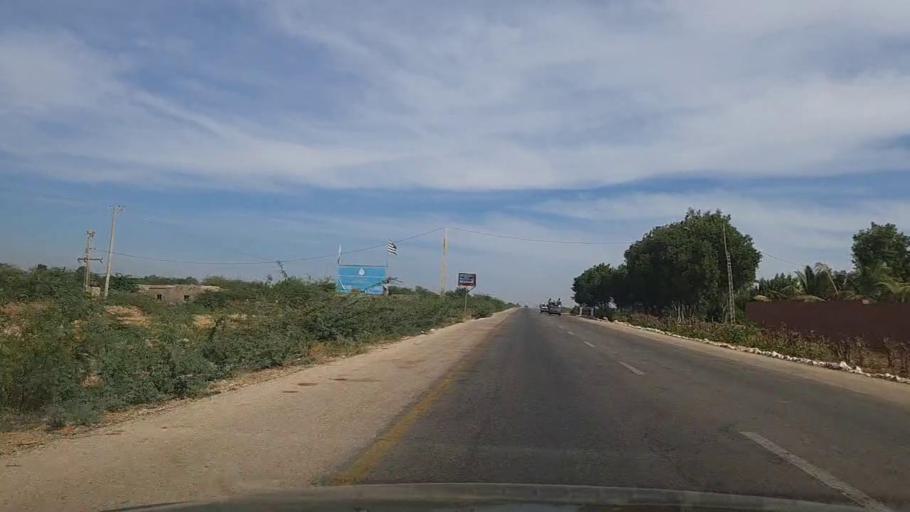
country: PK
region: Sindh
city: Thatta
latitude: 24.8312
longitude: 67.9961
